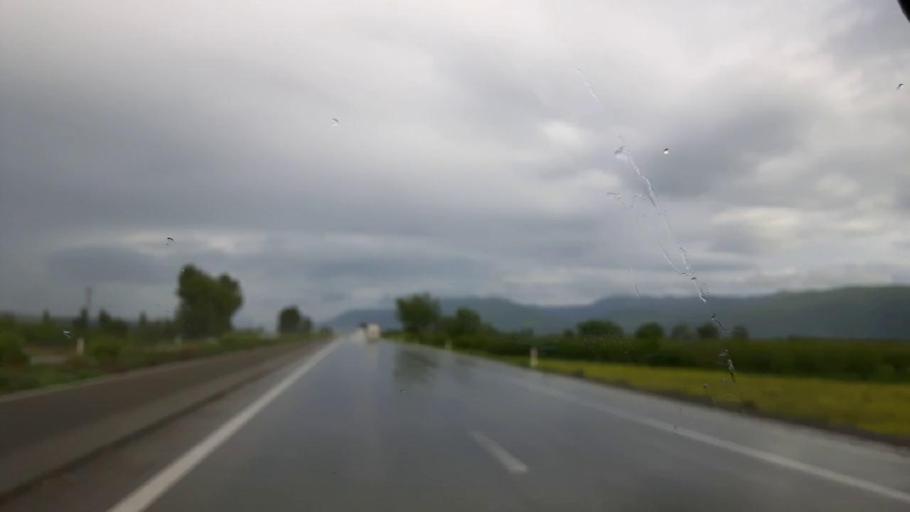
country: GE
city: Agara
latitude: 42.0376
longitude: 43.9362
